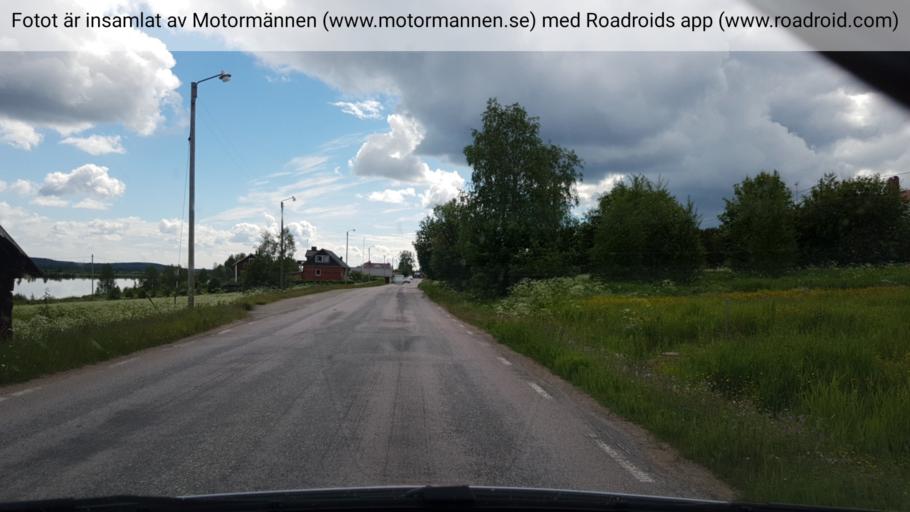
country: FI
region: Lapland
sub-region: Torniolaakso
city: Ylitornio
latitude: 66.2306
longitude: 23.6828
